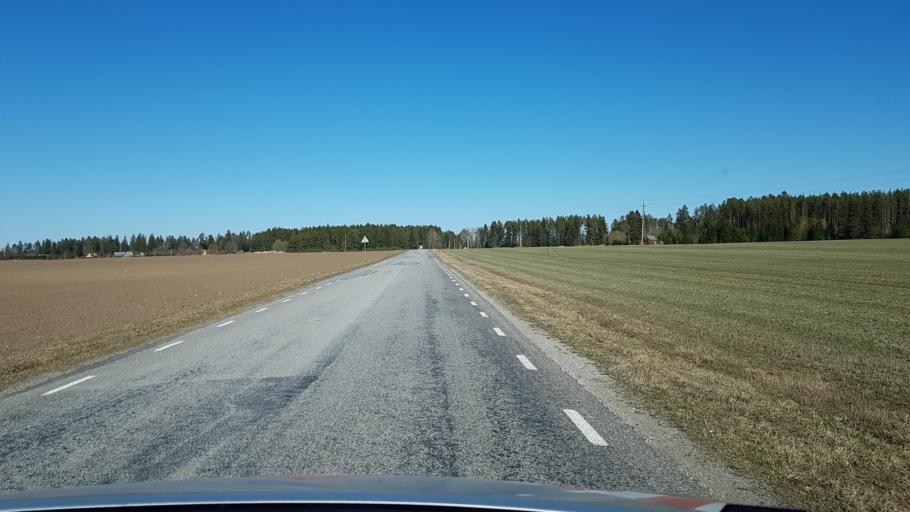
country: EE
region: Laeaene-Virumaa
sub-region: Viru-Nigula vald
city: Kunda
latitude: 59.4039
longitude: 26.5181
